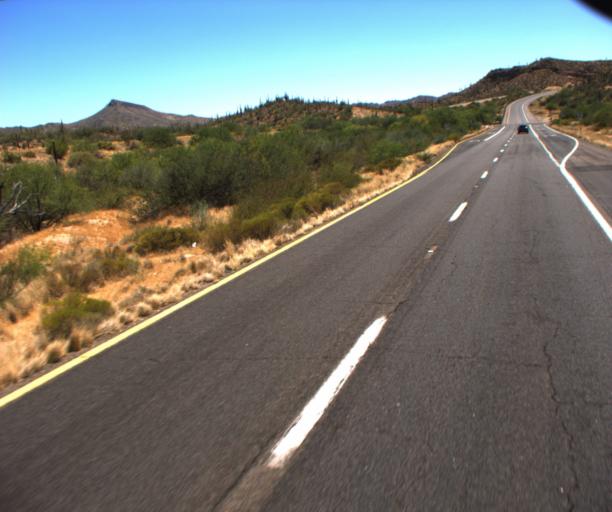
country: US
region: Arizona
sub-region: Maricopa County
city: Rio Verde
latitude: 33.7571
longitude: -111.4976
